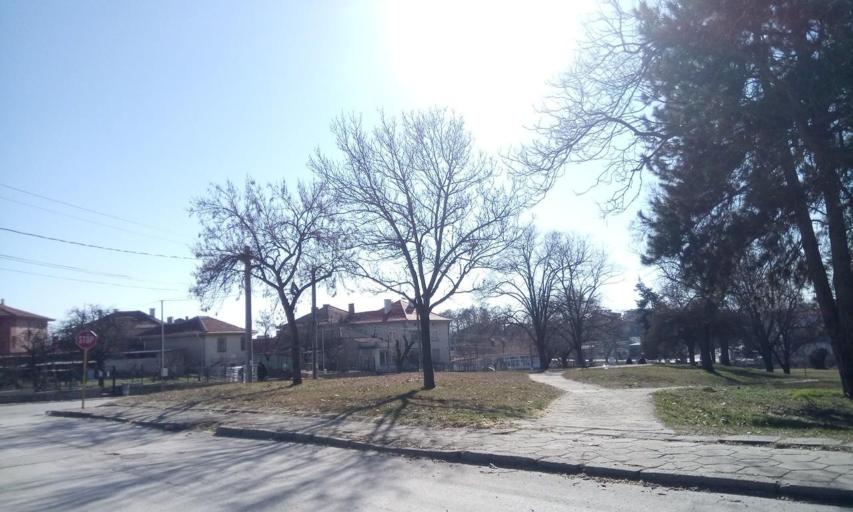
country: BG
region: Plovdiv
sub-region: Obshtina Khisarya
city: Khisarya
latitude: 42.5098
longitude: 24.7145
